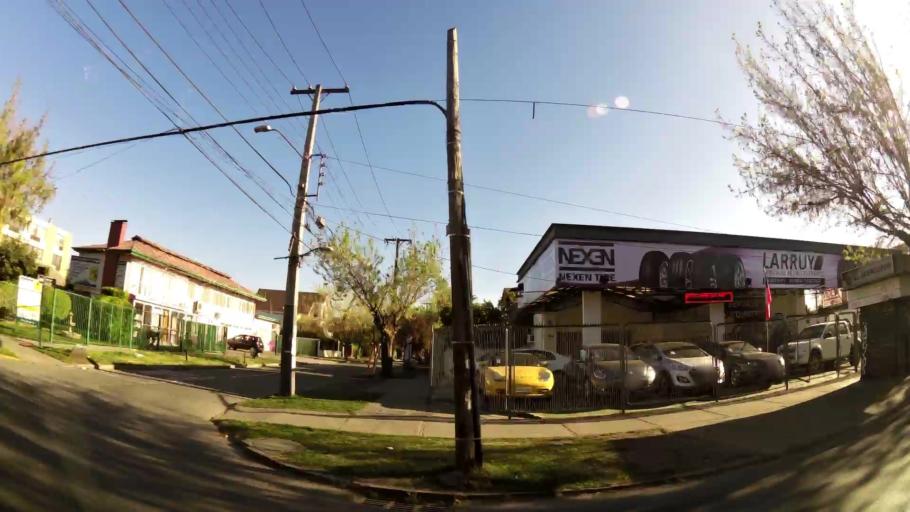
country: CL
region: Santiago Metropolitan
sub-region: Provincia de Santiago
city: Villa Presidente Frei, Nunoa, Santiago, Chile
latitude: -33.4523
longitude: -70.5606
